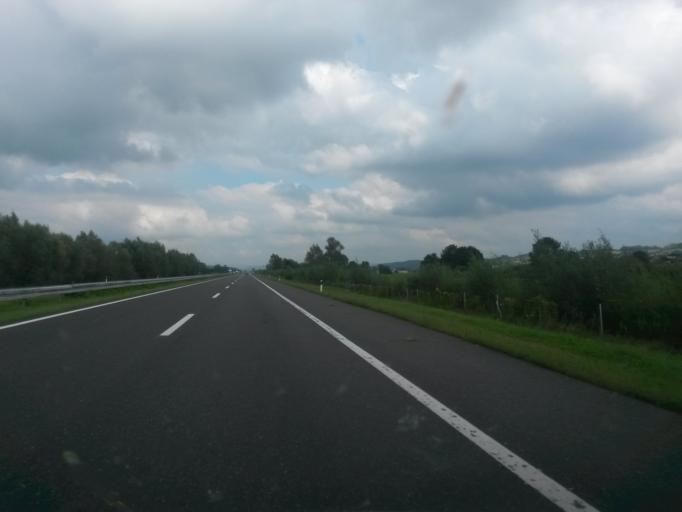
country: HR
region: Zagrebacka
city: Brckovljani
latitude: 45.9733
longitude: 16.2846
